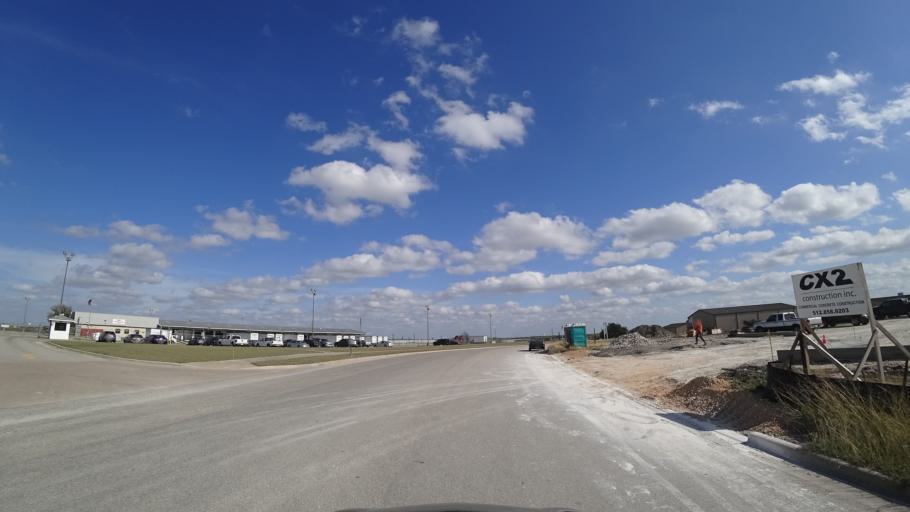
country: US
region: Texas
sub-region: Travis County
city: Windemere
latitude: 30.4614
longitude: -97.6627
